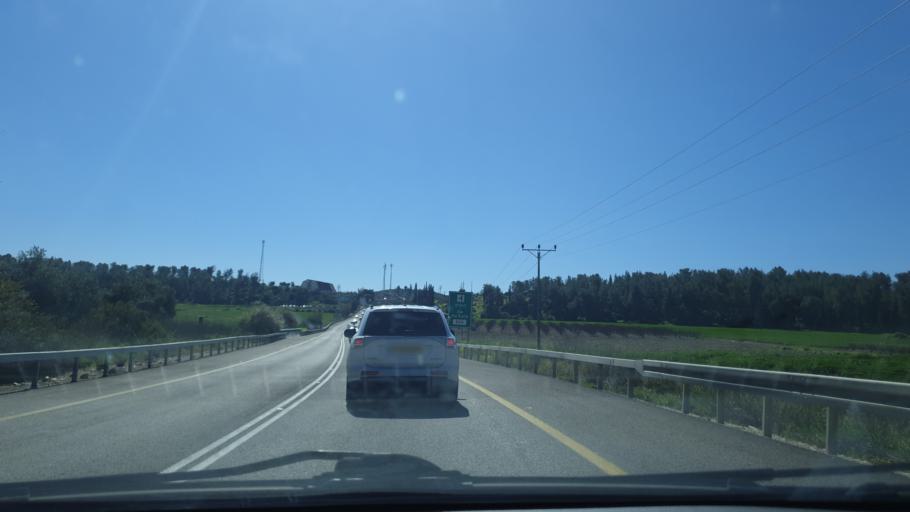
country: IL
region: Jerusalem
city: Bet Shemesh
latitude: 31.6918
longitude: 34.9435
